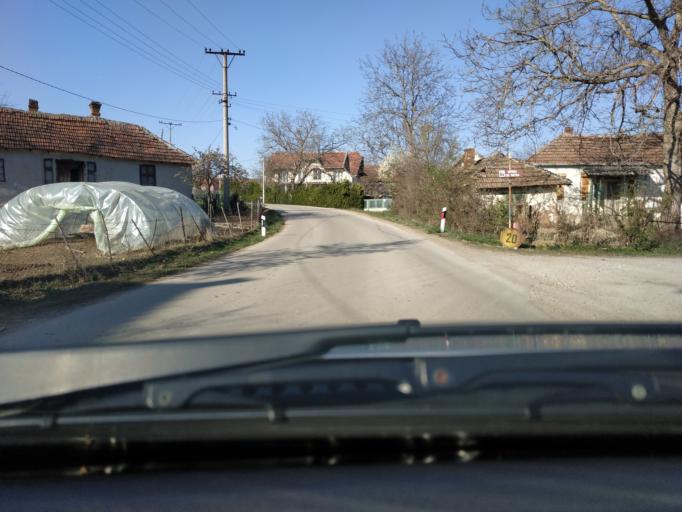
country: RS
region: Central Serbia
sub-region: Nisavski Okrug
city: Aleksinac
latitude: 43.4957
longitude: 21.7857
